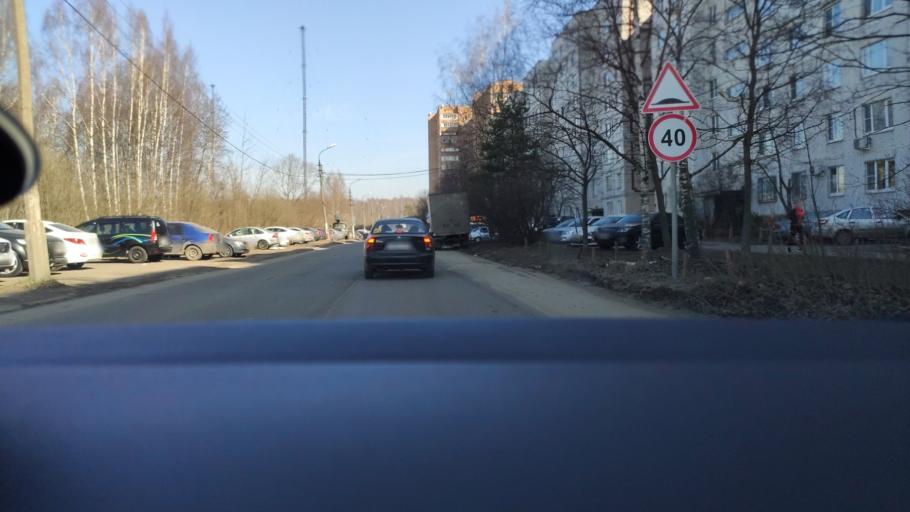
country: RU
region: Moskovskaya
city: Elektrostal'
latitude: 55.7711
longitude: 38.4181
